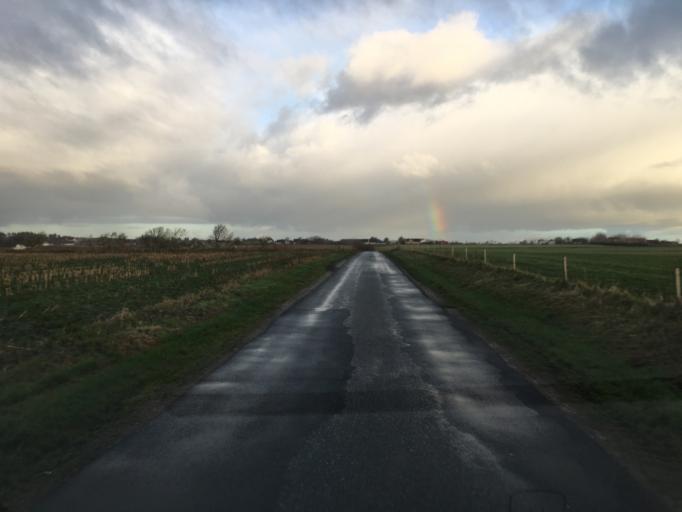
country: DK
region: South Denmark
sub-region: Tonder Kommune
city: Sherrebek
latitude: 55.1484
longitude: 8.8266
